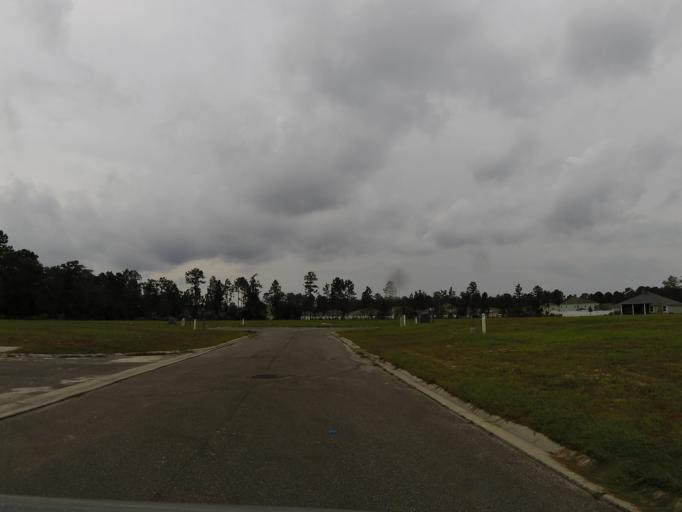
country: US
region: Florida
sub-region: Clay County
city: Middleburg
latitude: 30.1084
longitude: -81.8570
